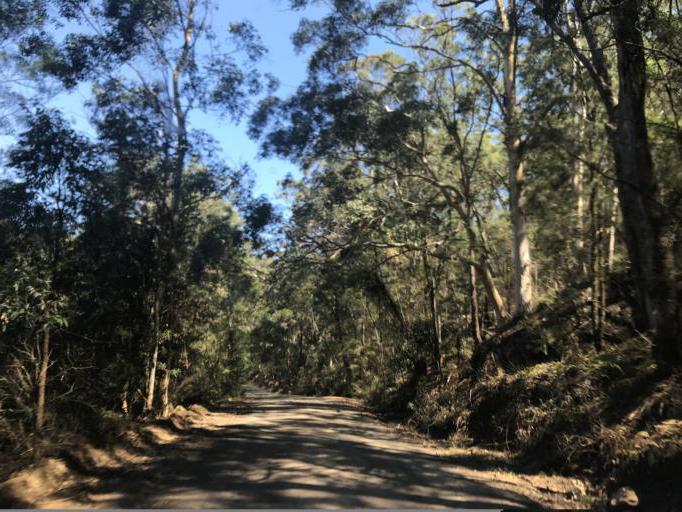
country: AU
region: New South Wales
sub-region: Wyong Shire
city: Little Jilliby
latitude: -33.1973
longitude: 151.0245
